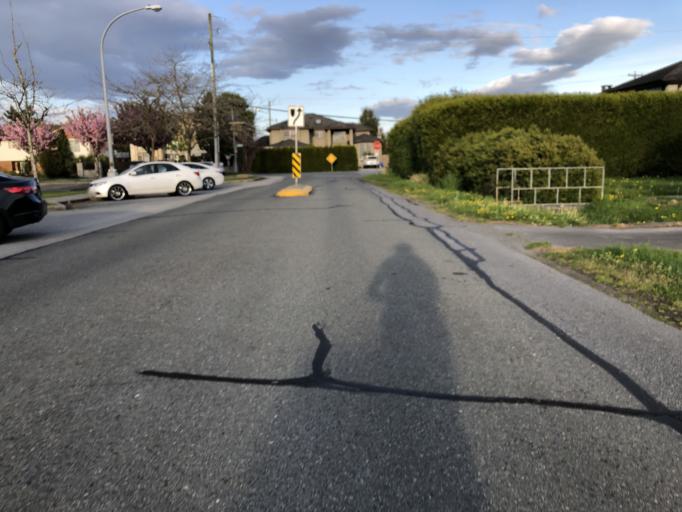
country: CA
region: British Columbia
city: Richmond
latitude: 49.1416
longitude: -123.1100
